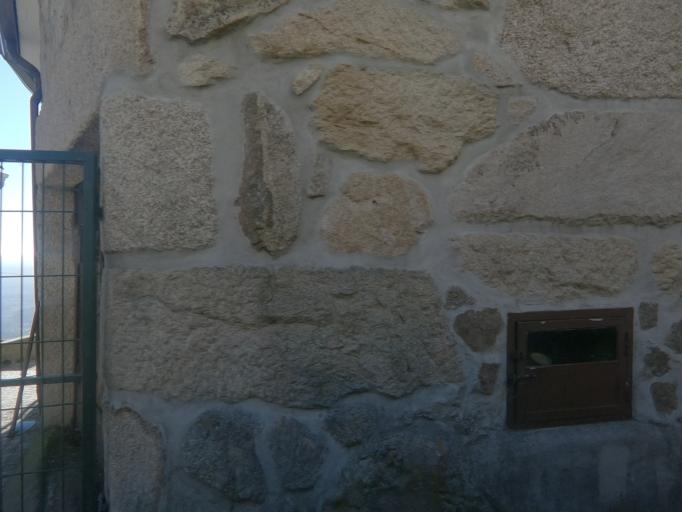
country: PT
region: Vila Real
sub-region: Vila Real
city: Vila Real
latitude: 41.3486
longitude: -7.7633
